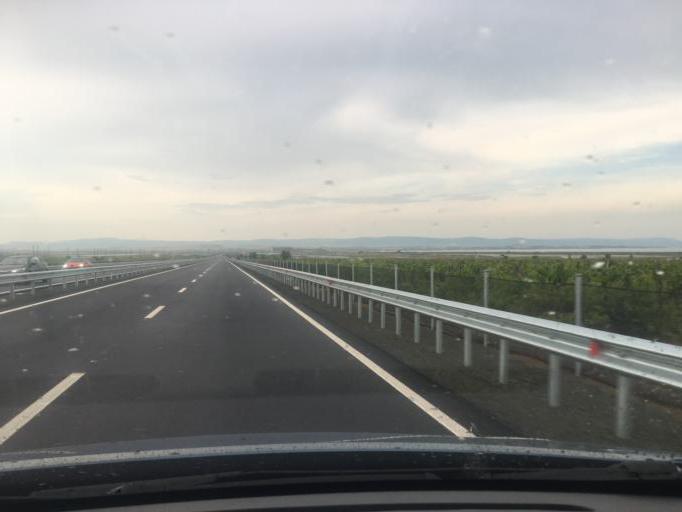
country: BG
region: Burgas
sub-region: Obshtina Pomorie
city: Pomorie
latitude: 42.6041
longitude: 27.6195
